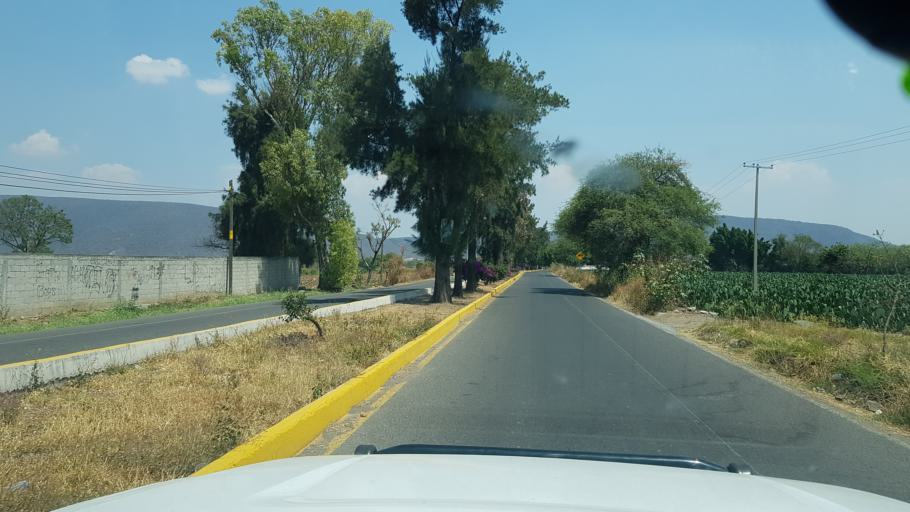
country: MX
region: Puebla
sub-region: Huaquechula
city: Cacaloxuchitl
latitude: 18.7927
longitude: -98.4647
